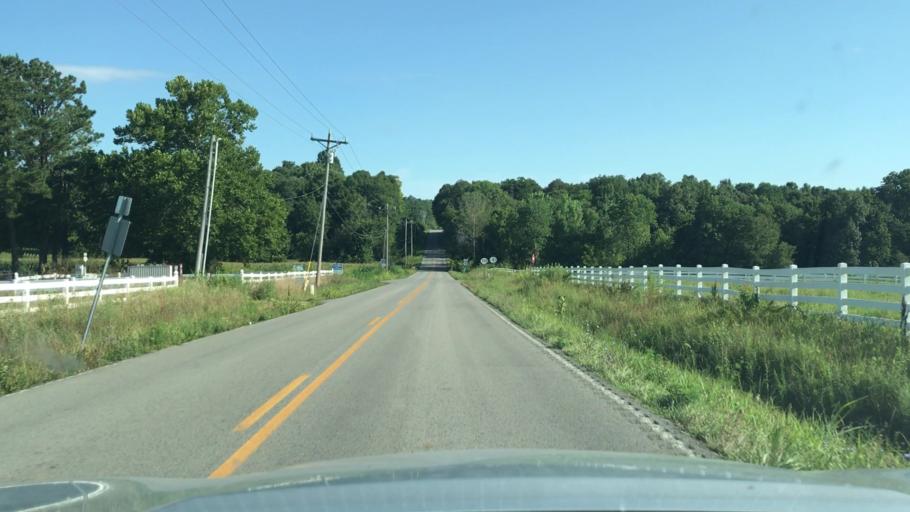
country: US
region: Kentucky
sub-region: Muhlenberg County
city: Greenville
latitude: 37.1009
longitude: -87.1263
